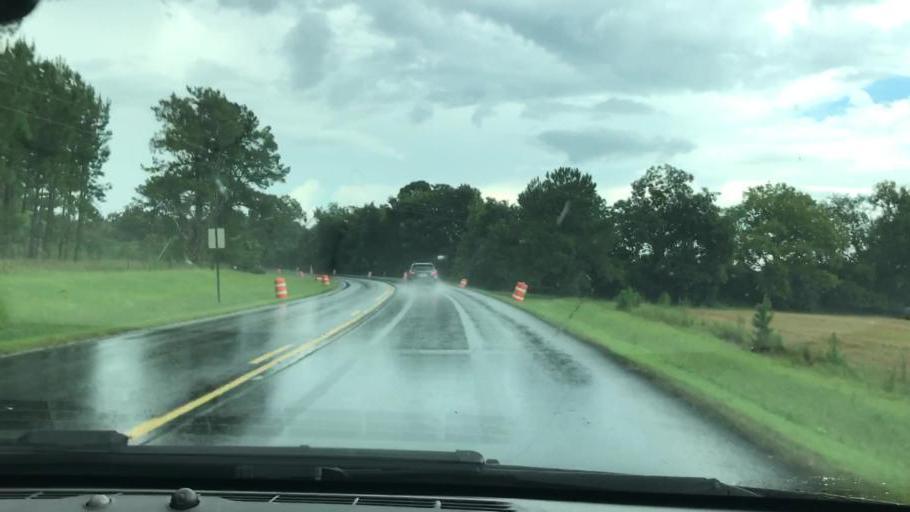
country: US
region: Georgia
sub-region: Clay County
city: Fort Gaines
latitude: 31.5646
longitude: -85.0185
